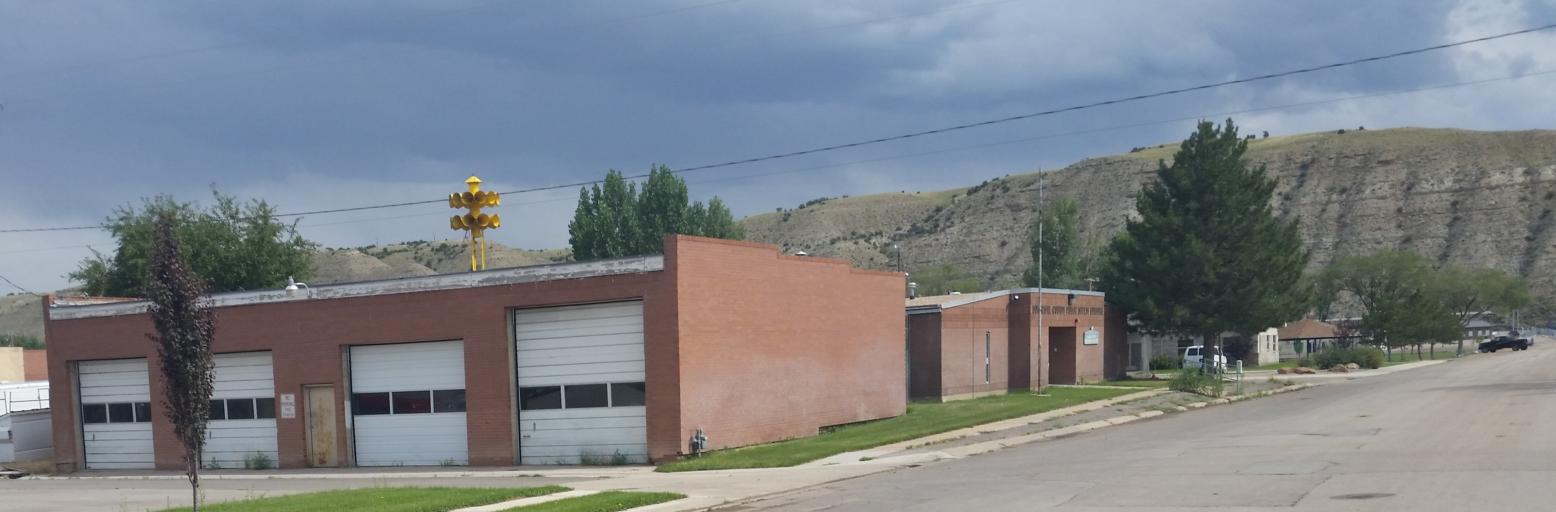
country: US
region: Utah
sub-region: Duchesne County
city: Duchesne
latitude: 40.1626
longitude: -110.4013
